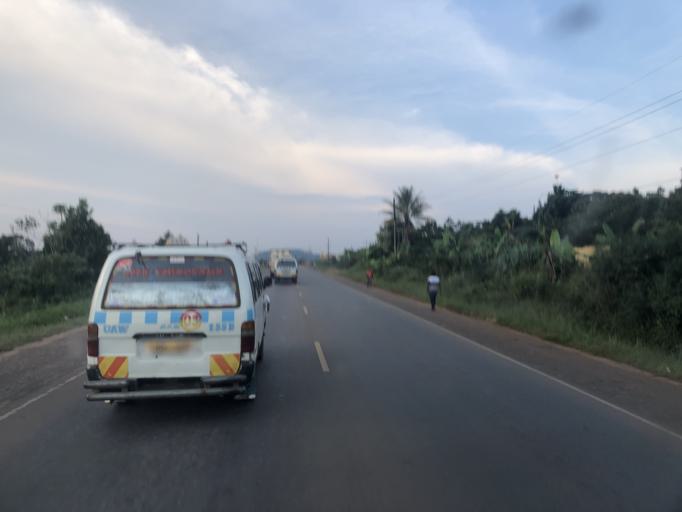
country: UG
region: Central Region
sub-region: Mpigi District
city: Mpigi
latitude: 0.2333
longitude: 32.3466
